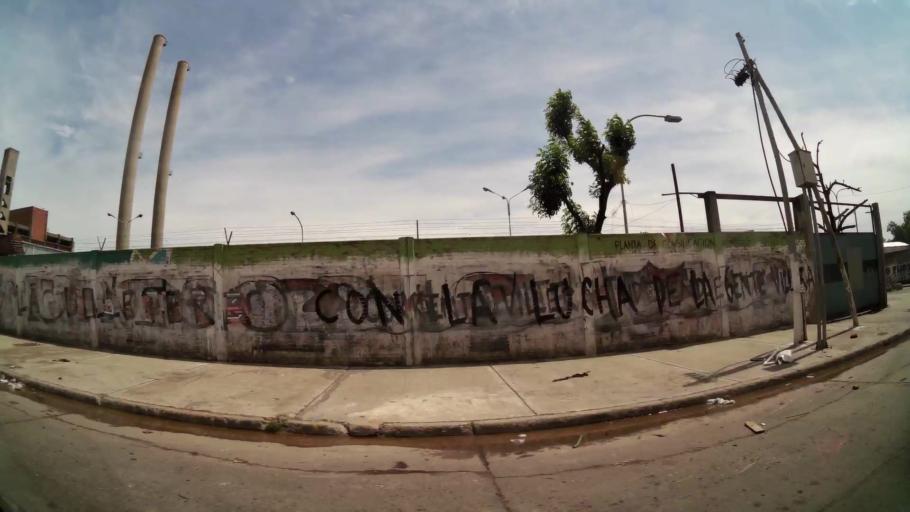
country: AR
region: Buenos Aires F.D.
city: Villa Lugano
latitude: -34.6534
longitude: -58.4413
